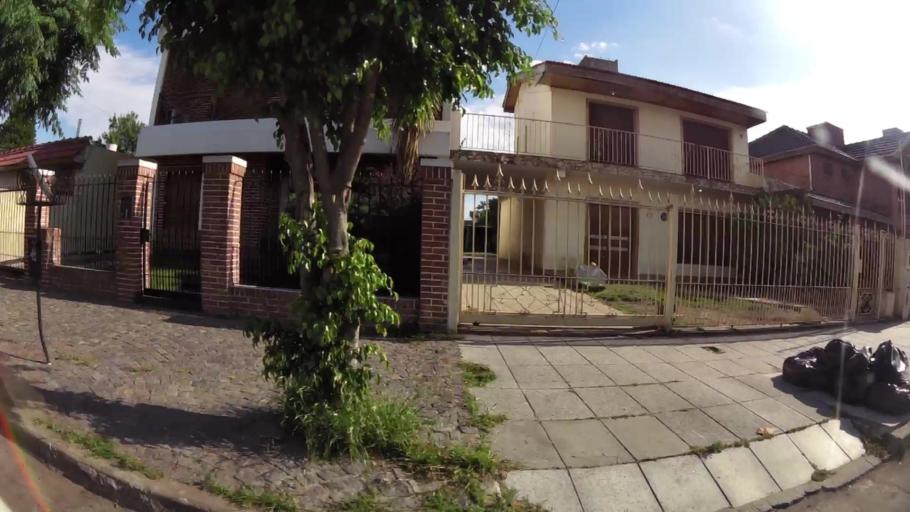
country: AR
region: Buenos Aires
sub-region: Partido de Merlo
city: Merlo
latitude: -34.6587
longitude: -58.7229
